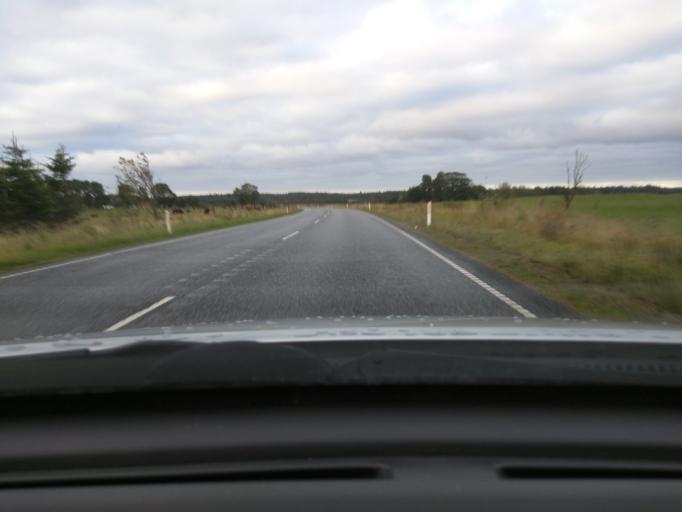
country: DK
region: Central Jutland
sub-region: Silkeborg Kommune
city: Kjellerup
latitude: 56.3336
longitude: 9.3390
